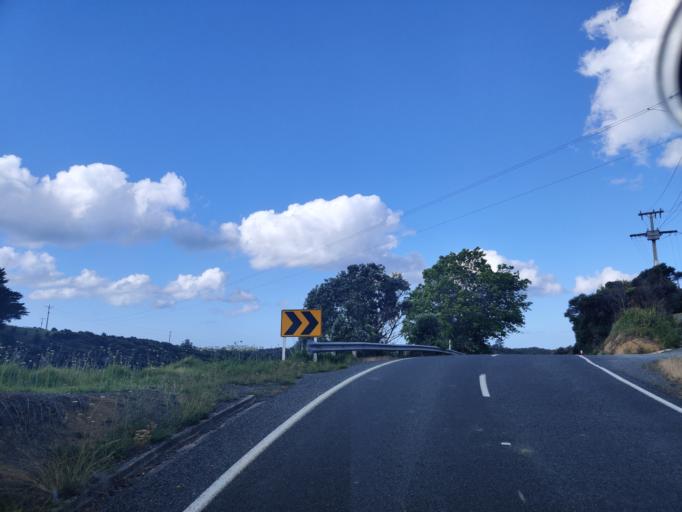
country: NZ
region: Northland
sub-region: Whangarei
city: Ngunguru
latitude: -35.6200
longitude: 174.5282
